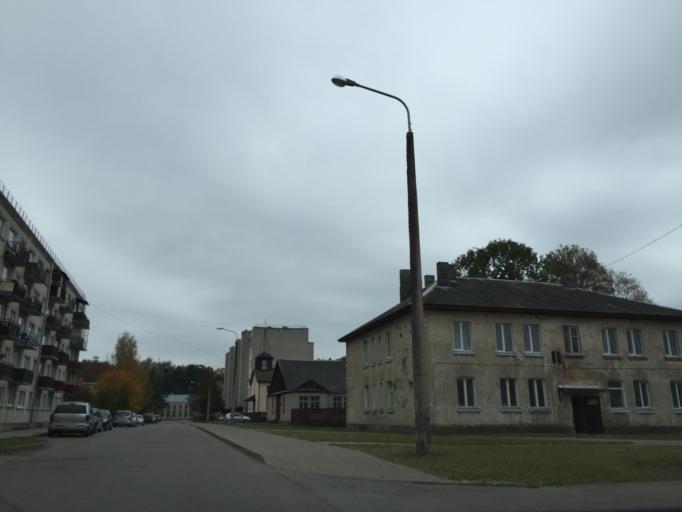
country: LV
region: Olaine
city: Olaine
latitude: 56.7878
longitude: 23.9367
